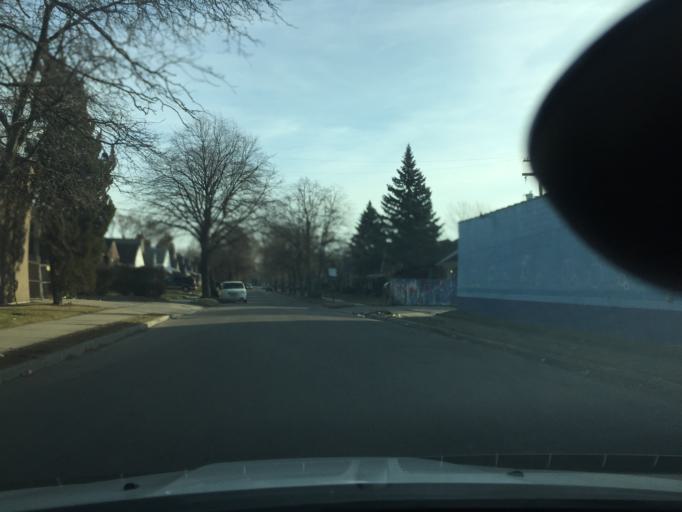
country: US
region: Michigan
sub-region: Macomb County
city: Eastpointe
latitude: 42.4339
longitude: -82.9653
